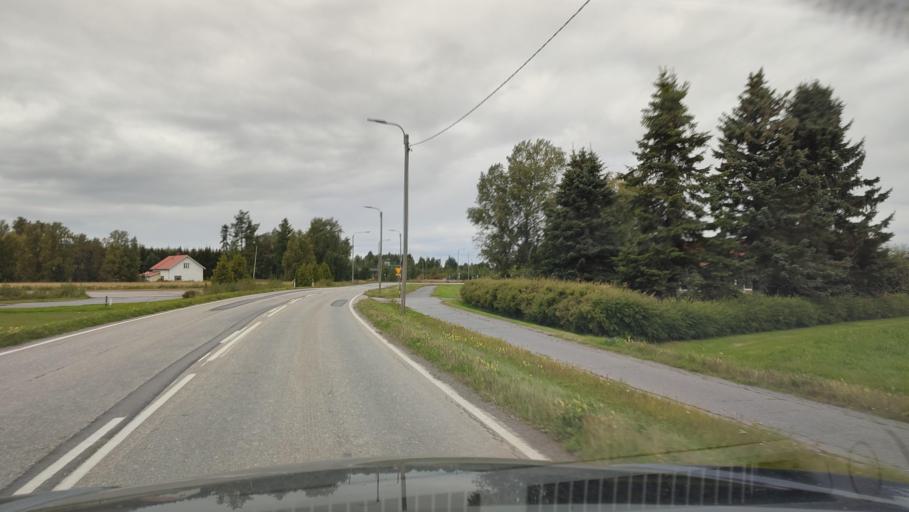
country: FI
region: Ostrobothnia
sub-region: Sydosterbotten
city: Kristinestad
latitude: 62.2586
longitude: 21.4929
